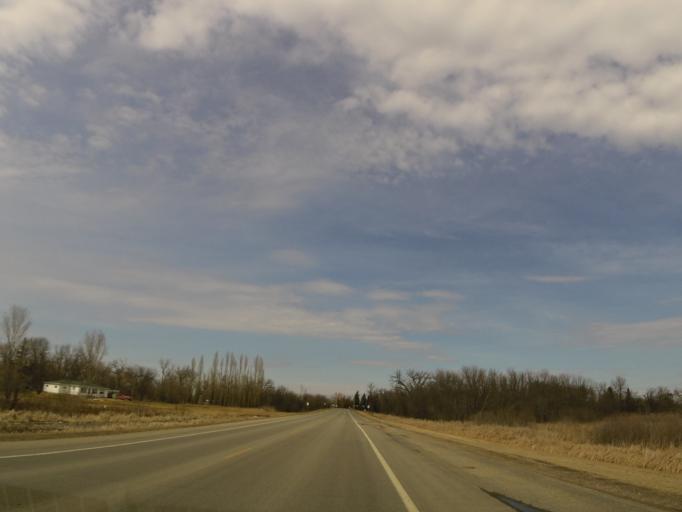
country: US
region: North Dakota
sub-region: Walsh County
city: Grafton
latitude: 48.2817
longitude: -97.3685
